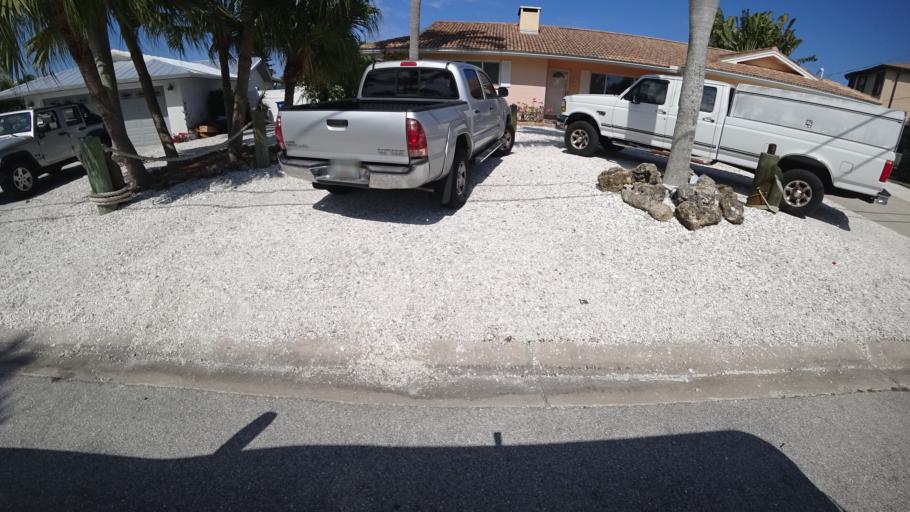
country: US
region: Florida
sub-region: Manatee County
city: Cortez
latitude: 27.4599
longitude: -82.6560
